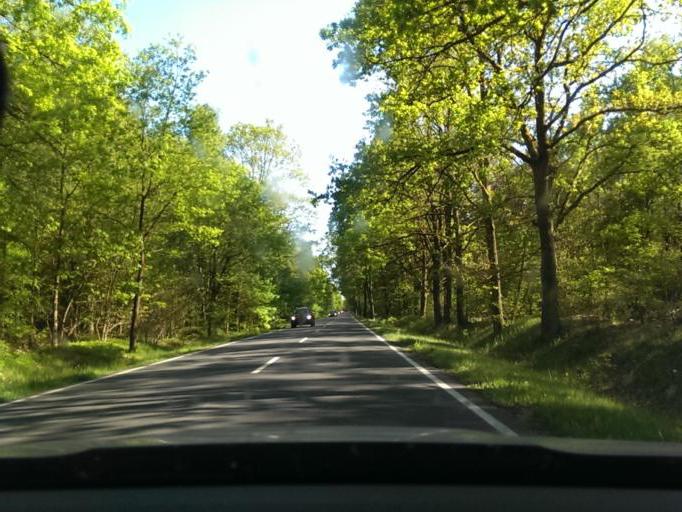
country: DE
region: Lower Saxony
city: Hambuhren
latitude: 52.6282
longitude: 9.9299
